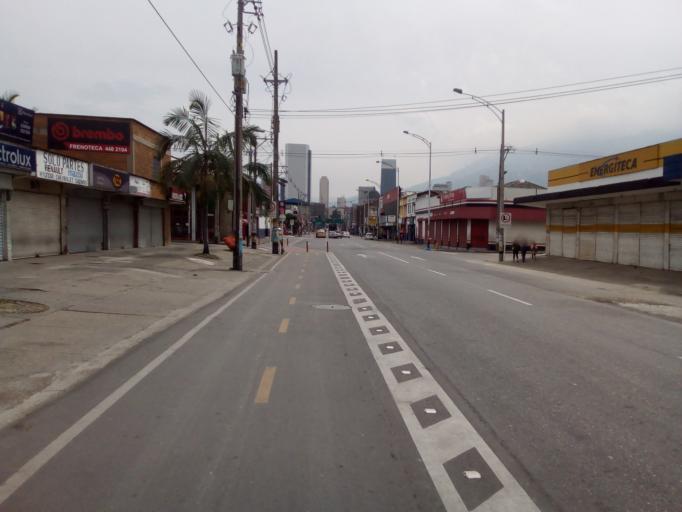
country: CO
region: Antioquia
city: Medellin
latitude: 6.2403
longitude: -75.5716
